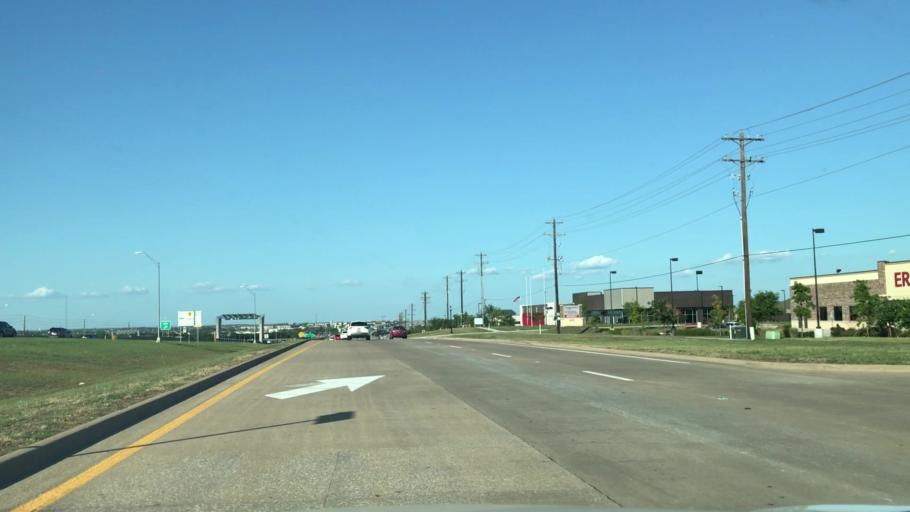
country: US
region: Texas
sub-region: Collin County
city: Frisco
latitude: 33.1124
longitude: -96.7659
